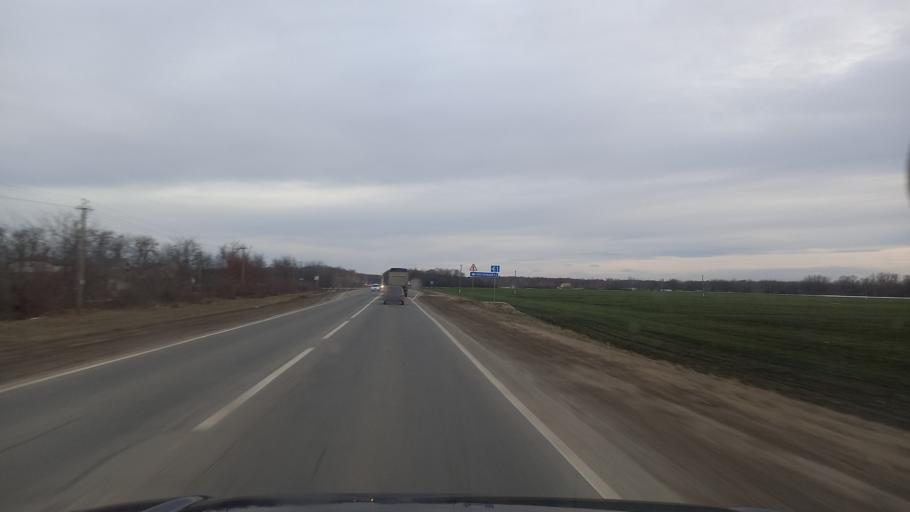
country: RU
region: Krasnodarskiy
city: Yuzhnyy
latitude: 44.7438
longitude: 39.9306
